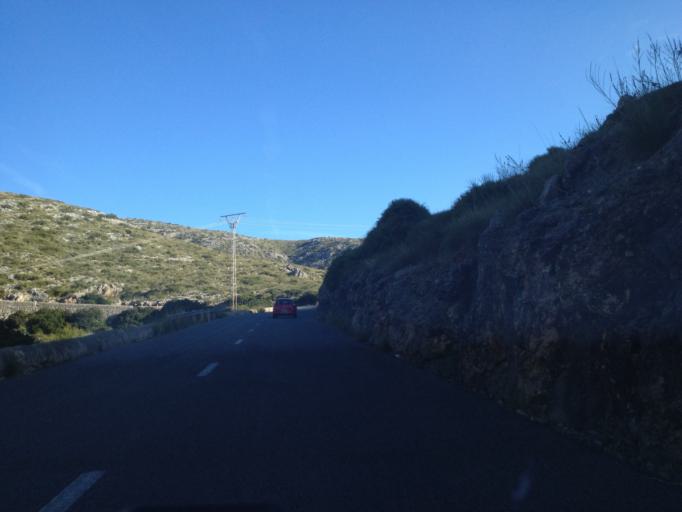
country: ES
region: Balearic Islands
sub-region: Illes Balears
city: Alcudia
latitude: 39.9155
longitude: 3.1069
